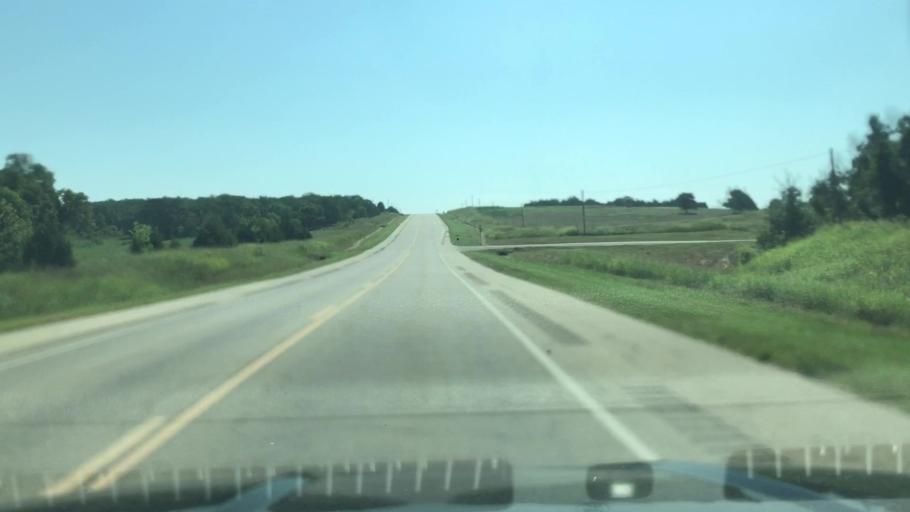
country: US
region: Oklahoma
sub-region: Creek County
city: Mannford
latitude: 36.0031
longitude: -96.4236
